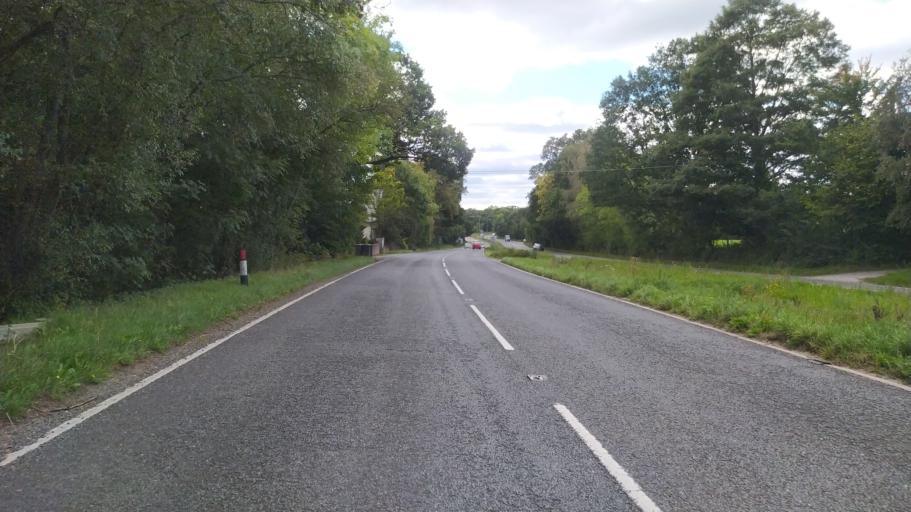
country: GB
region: England
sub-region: Hampshire
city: Romsey
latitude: 50.9571
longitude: -1.5303
